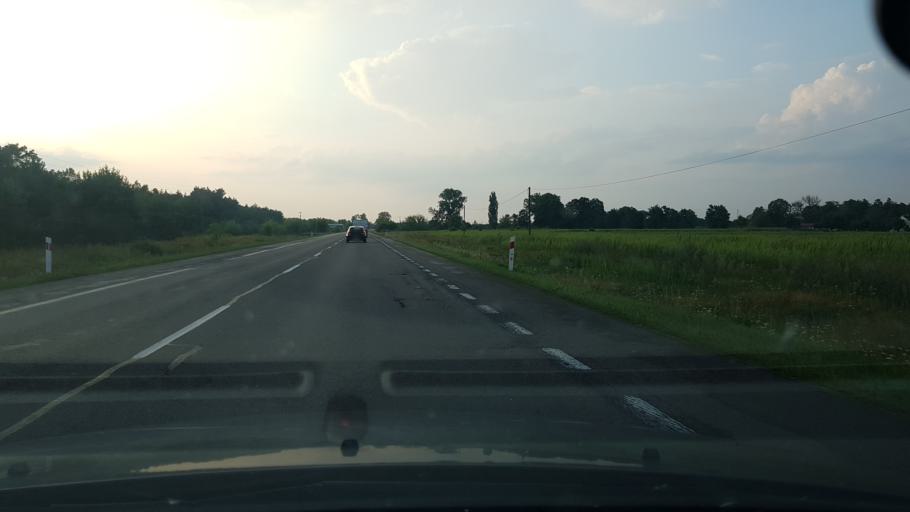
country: PL
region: Masovian Voivodeship
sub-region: Powiat ciechanowski
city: Glinojeck
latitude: 52.7733
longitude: 20.2924
